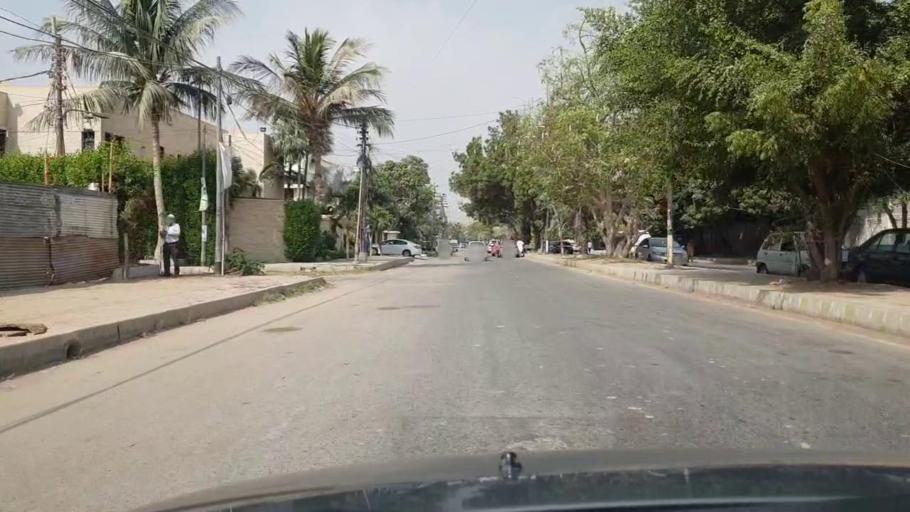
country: PK
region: Sindh
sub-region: Karachi District
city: Karachi
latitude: 24.8723
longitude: 67.0881
